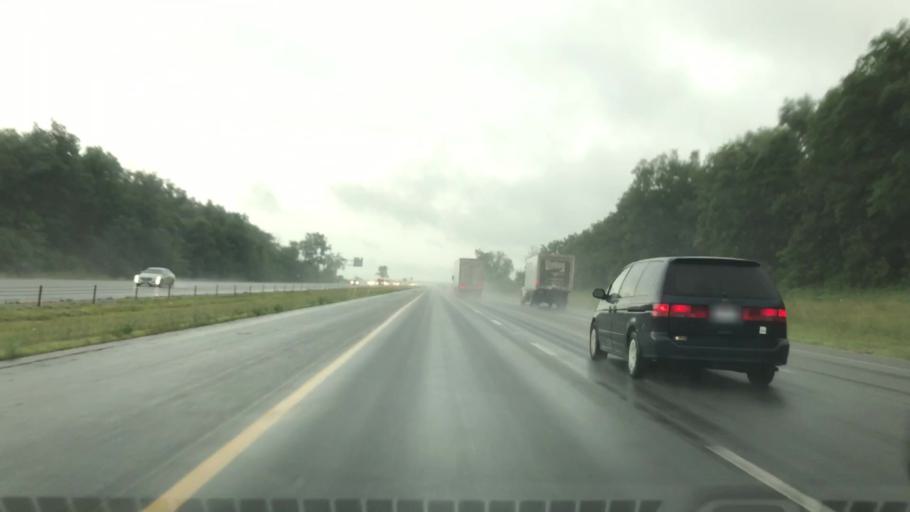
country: US
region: Ohio
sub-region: Madison County
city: Choctaw Lake
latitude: 39.9420
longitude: -83.4901
